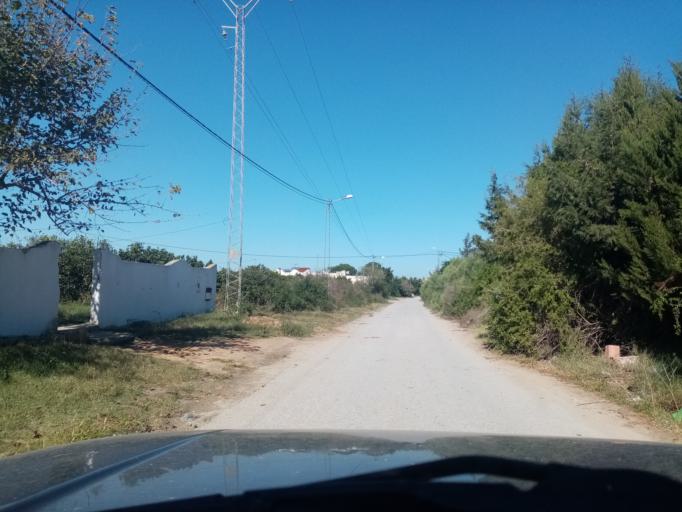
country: TN
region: Nabul
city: Bu `Urqub
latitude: 36.5710
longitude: 10.5758
